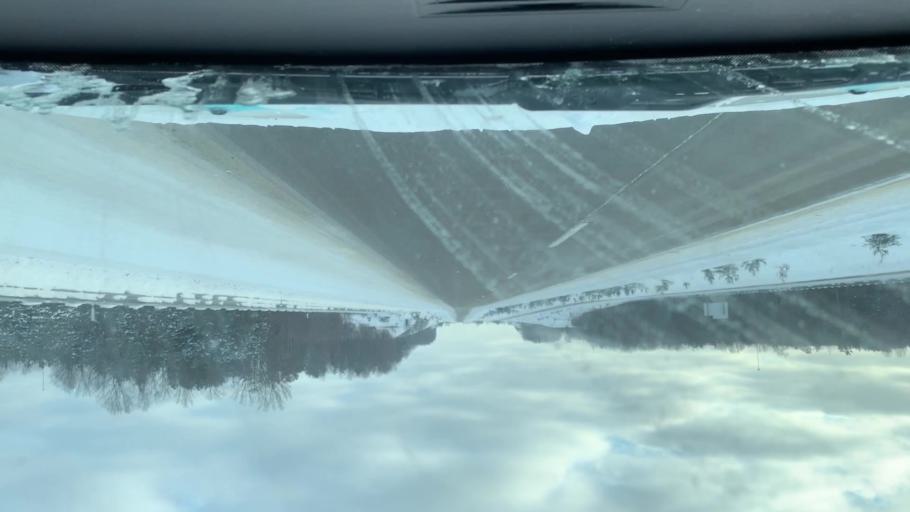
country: US
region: Michigan
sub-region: Wexford County
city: Manton
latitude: 44.4016
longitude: -85.3819
